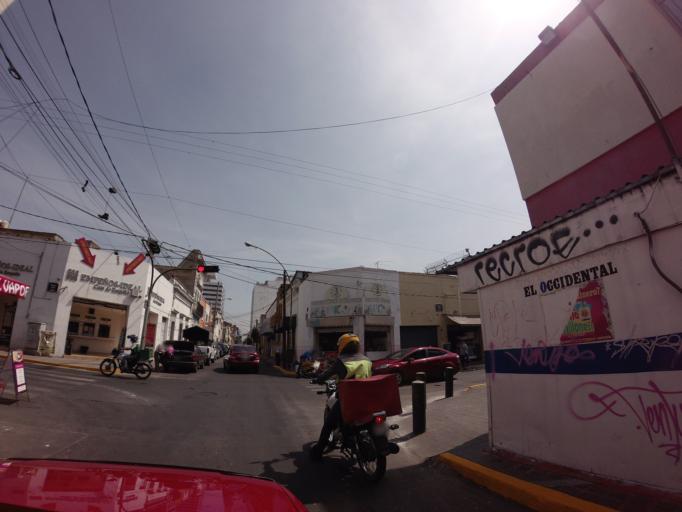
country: MX
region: Jalisco
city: Guadalajara
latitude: 20.6827
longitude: -103.3468
